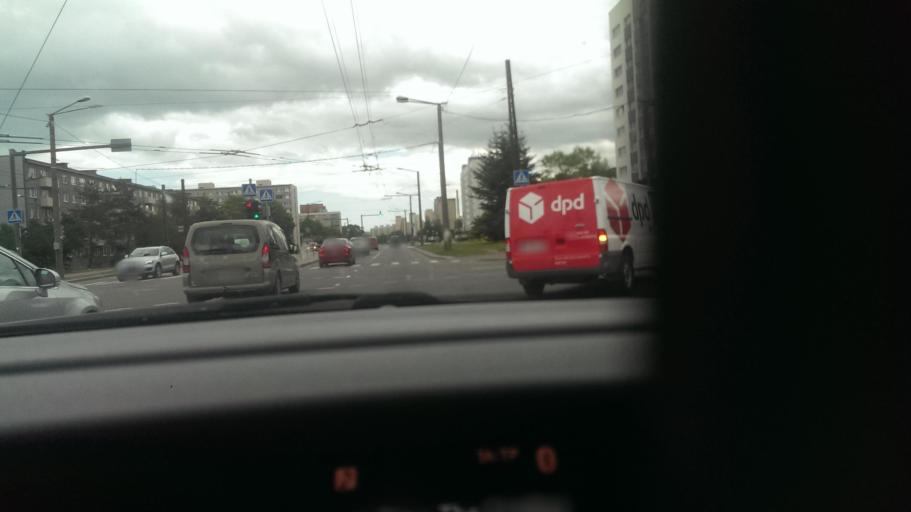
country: EE
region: Harju
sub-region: Saue vald
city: Laagri
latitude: 59.3985
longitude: 24.6805
